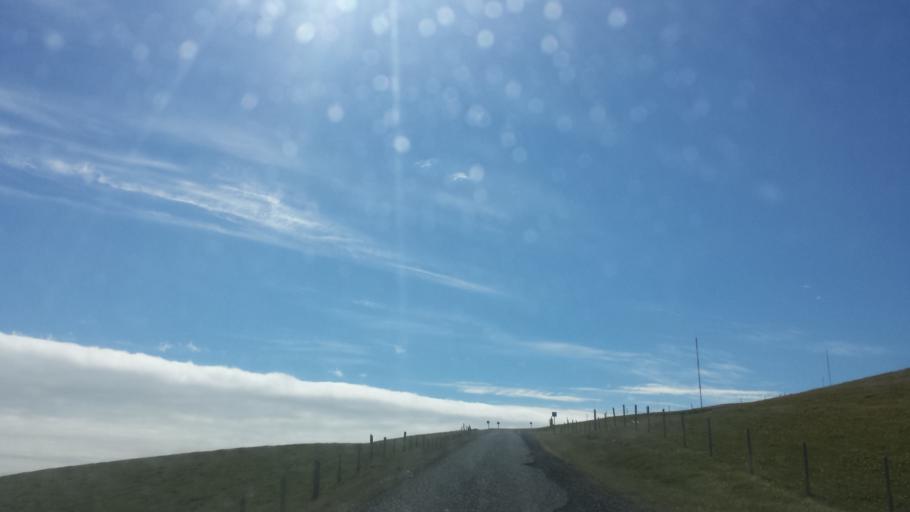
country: IS
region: South
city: Vestmannaeyjar
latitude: 63.4014
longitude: -20.2822
